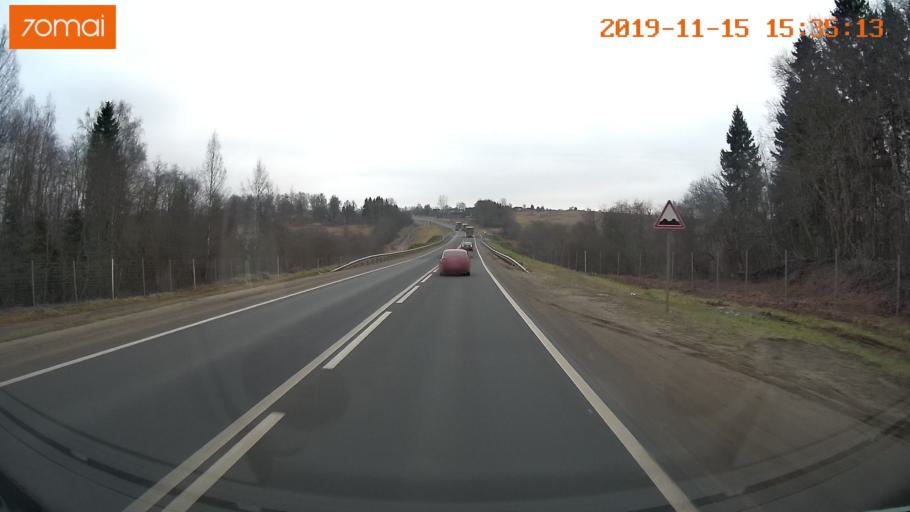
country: RU
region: Jaroslavl
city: Danilov
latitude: 58.0615
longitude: 40.0881
